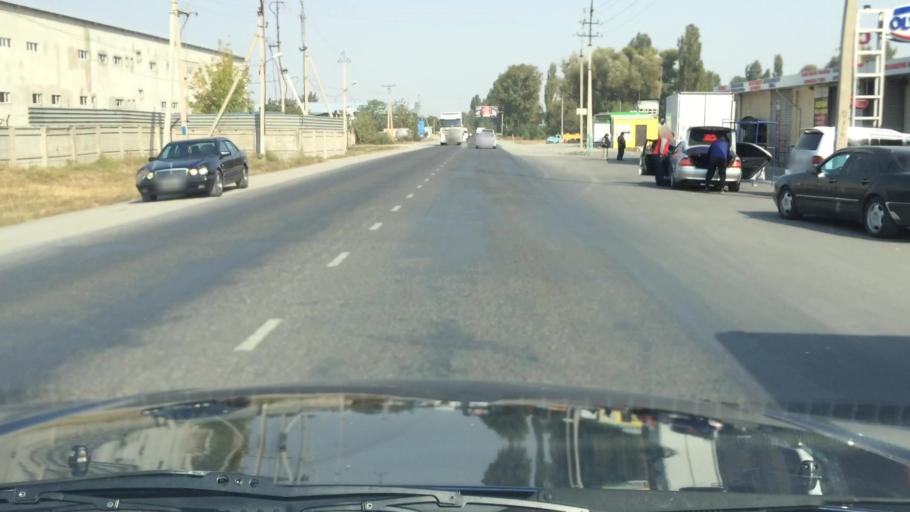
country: KG
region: Chuy
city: Lebedinovka
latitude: 42.8898
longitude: 74.6796
